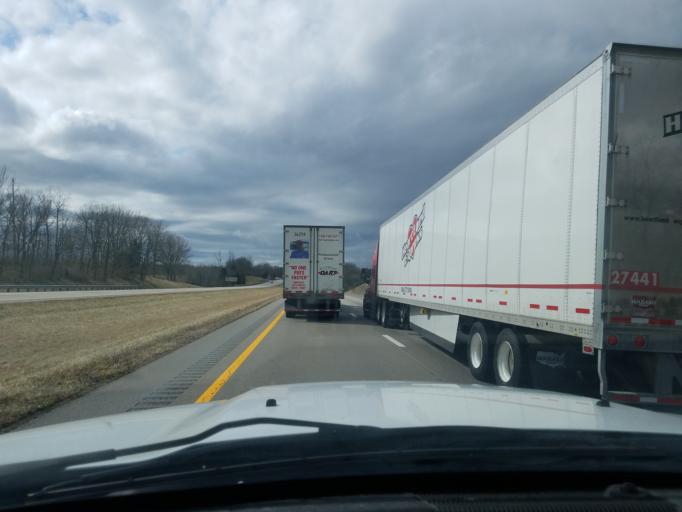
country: US
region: Kentucky
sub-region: Montgomery County
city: Mount Sterling
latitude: 38.0929
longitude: -83.8748
